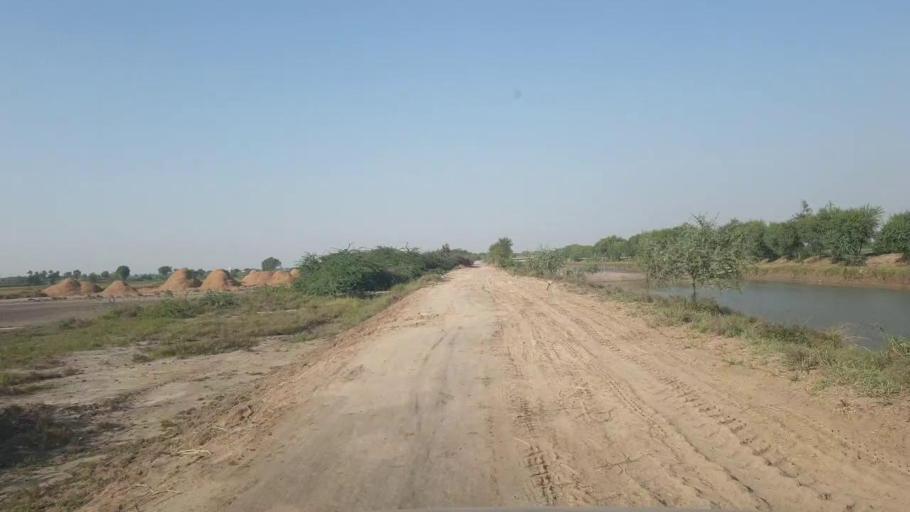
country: PK
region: Sindh
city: Badin
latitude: 24.6359
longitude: 68.8150
